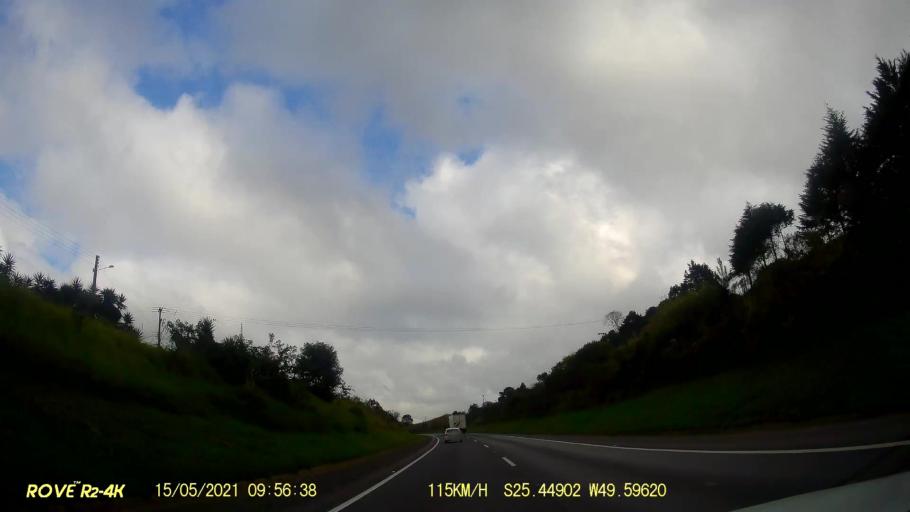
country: BR
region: Parana
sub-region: Campo Largo
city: Campo Largo
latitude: -25.4486
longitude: -49.5967
